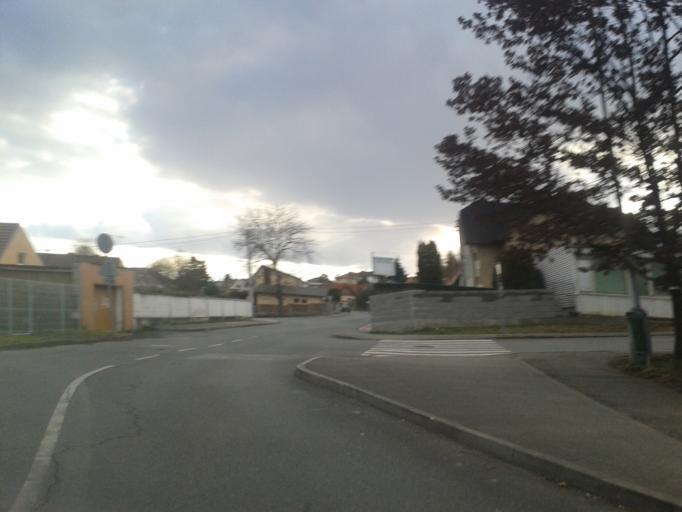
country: CZ
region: Central Bohemia
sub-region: Okres Beroun
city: Kraluv Dvur
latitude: 49.9446
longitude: 14.0255
